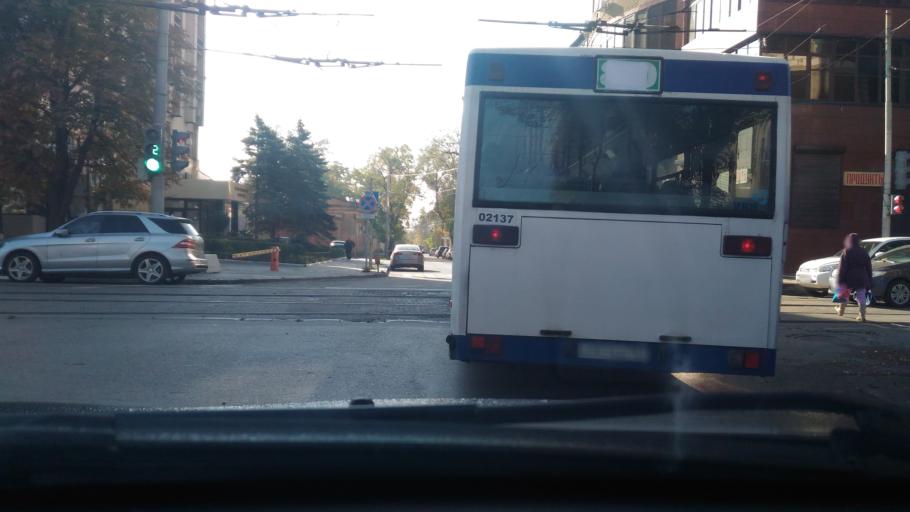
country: RU
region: Rostov
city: Rostov-na-Donu
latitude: 47.2290
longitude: 39.7628
